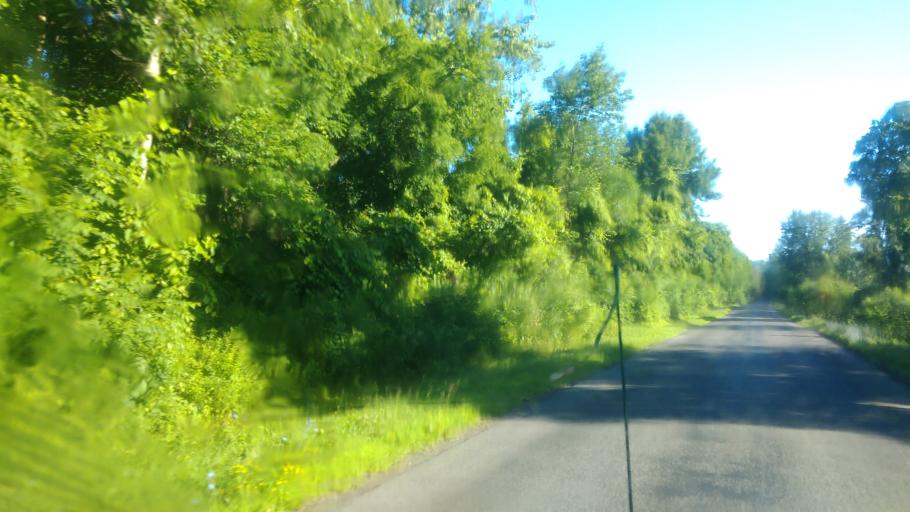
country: US
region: New York
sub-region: Wayne County
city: Lyons
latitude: 43.1254
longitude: -77.0386
